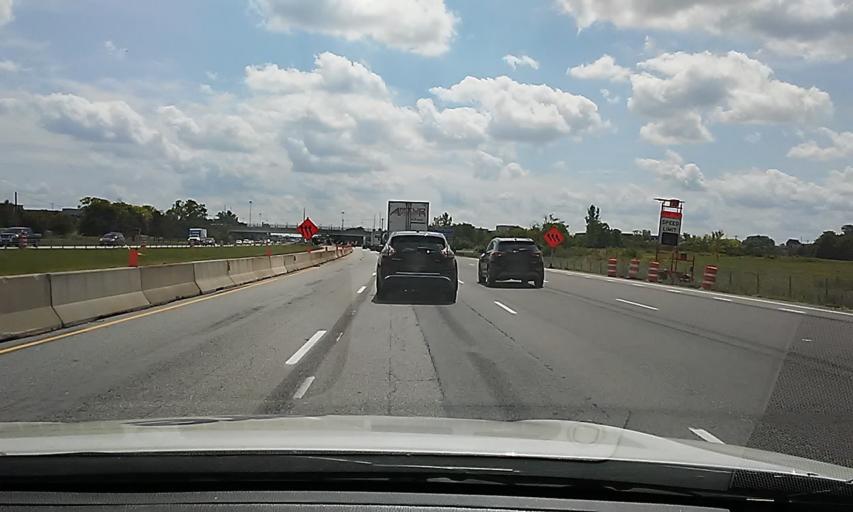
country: US
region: Ohio
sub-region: Franklin County
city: Dublin
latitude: 40.0866
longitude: -83.1386
